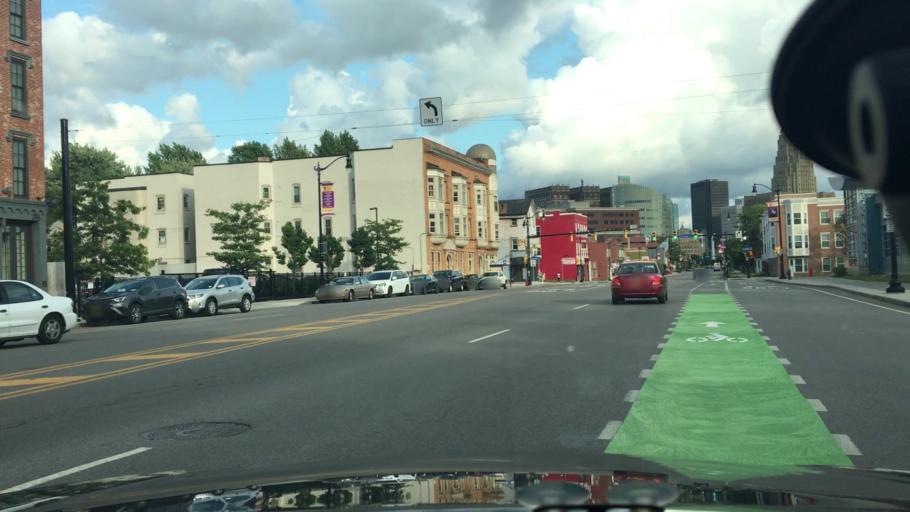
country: US
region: New York
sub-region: Erie County
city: Buffalo
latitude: 42.8926
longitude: -78.8841
